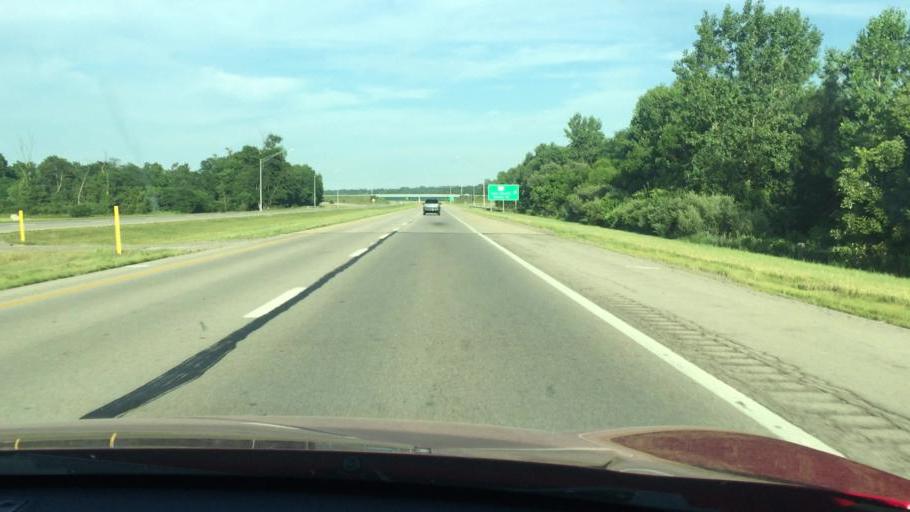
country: US
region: Ohio
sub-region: Logan County
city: Bellefontaine
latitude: 40.3272
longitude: -83.6721
